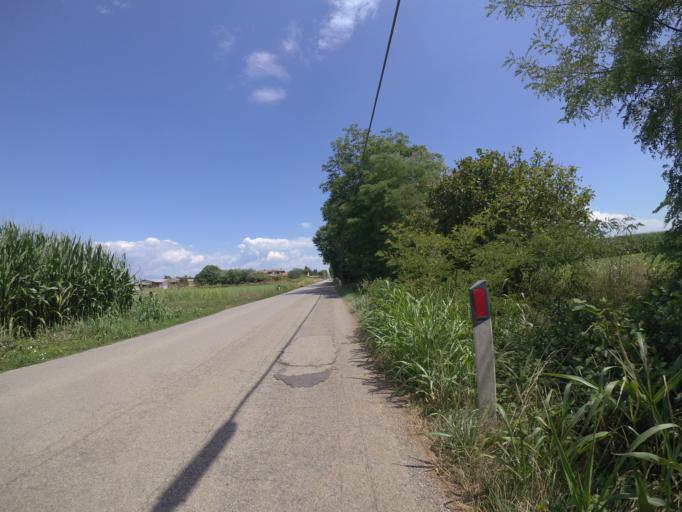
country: IT
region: Friuli Venezia Giulia
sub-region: Provincia di Udine
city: Lestizza
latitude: 45.9726
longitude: 13.1261
